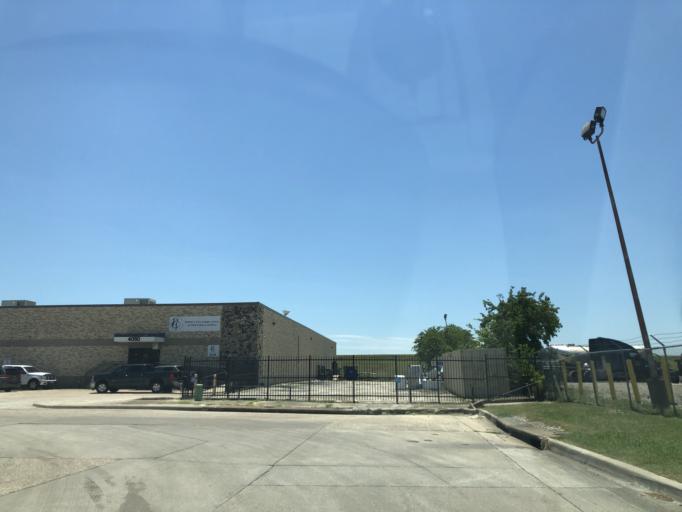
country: US
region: Texas
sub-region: Dallas County
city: Irving
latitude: 32.8042
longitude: -96.8860
